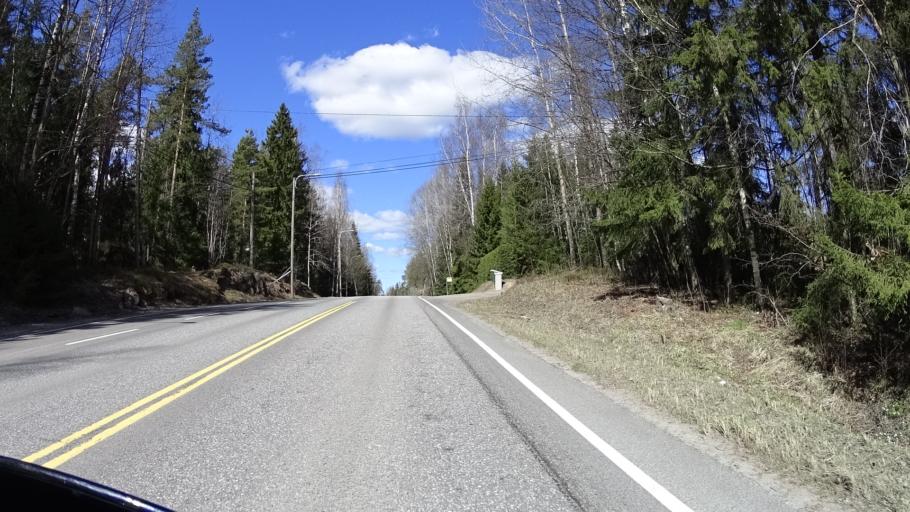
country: FI
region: Uusimaa
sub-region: Helsinki
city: Kirkkonummi
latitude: 60.2549
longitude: 24.5045
